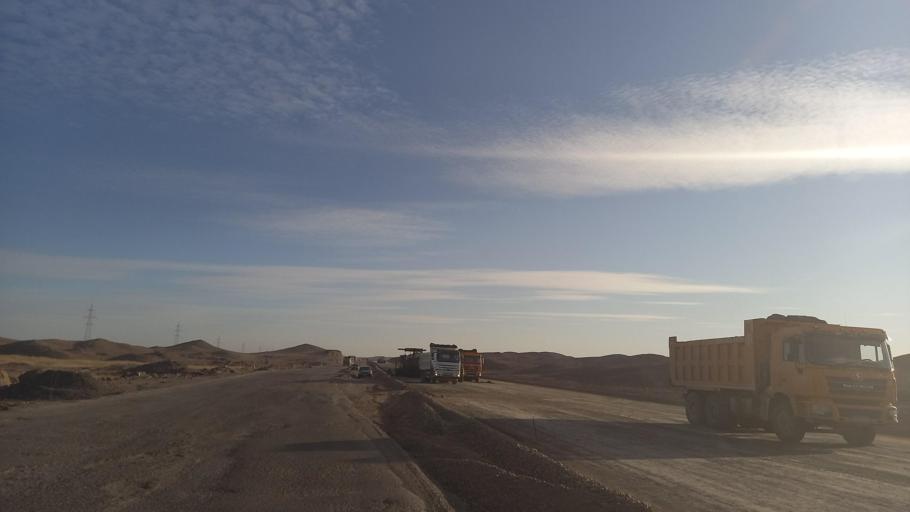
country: KZ
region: Zhambyl
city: Mynaral
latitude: 45.3897
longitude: 73.6474
